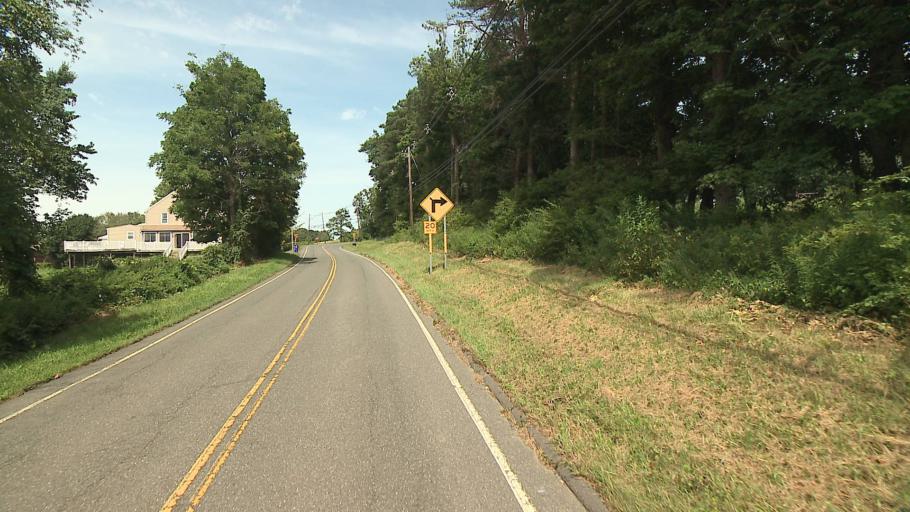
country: US
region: Connecticut
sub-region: Litchfield County
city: Bethlehem Village
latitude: 41.6184
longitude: -73.2453
